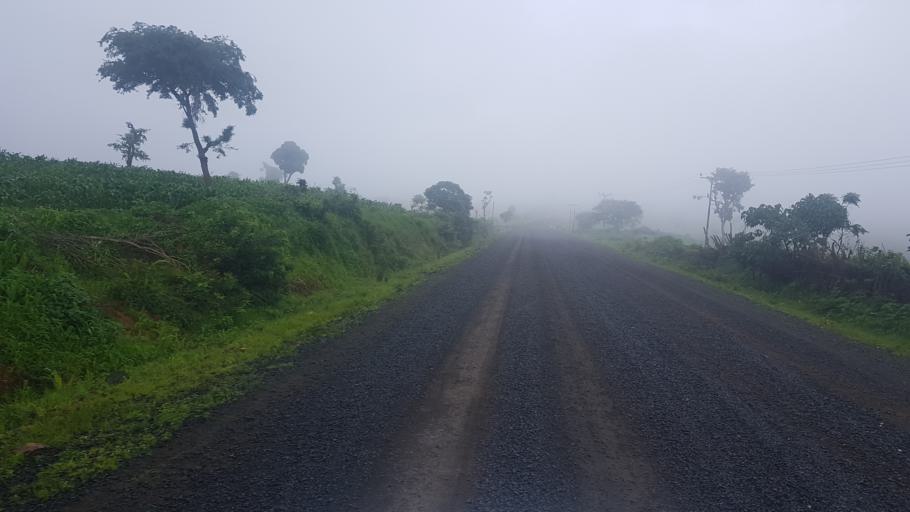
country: ET
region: Amhara
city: Bure
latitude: 10.1971
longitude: 36.9766
